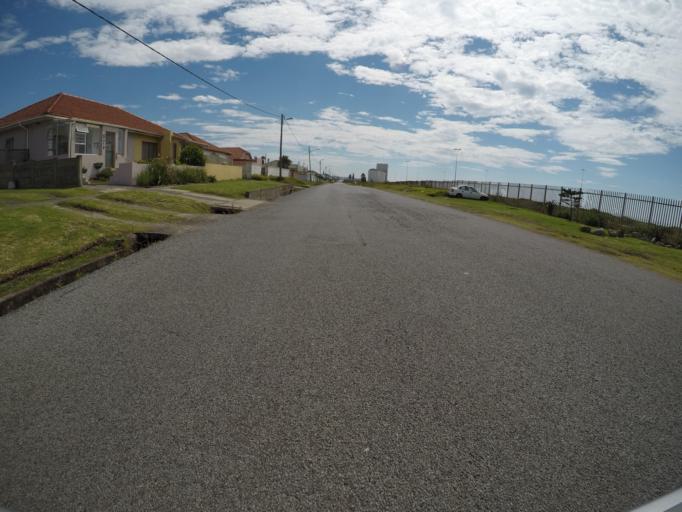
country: ZA
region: Eastern Cape
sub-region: Buffalo City Metropolitan Municipality
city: East London
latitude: -33.0377
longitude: 27.9064
